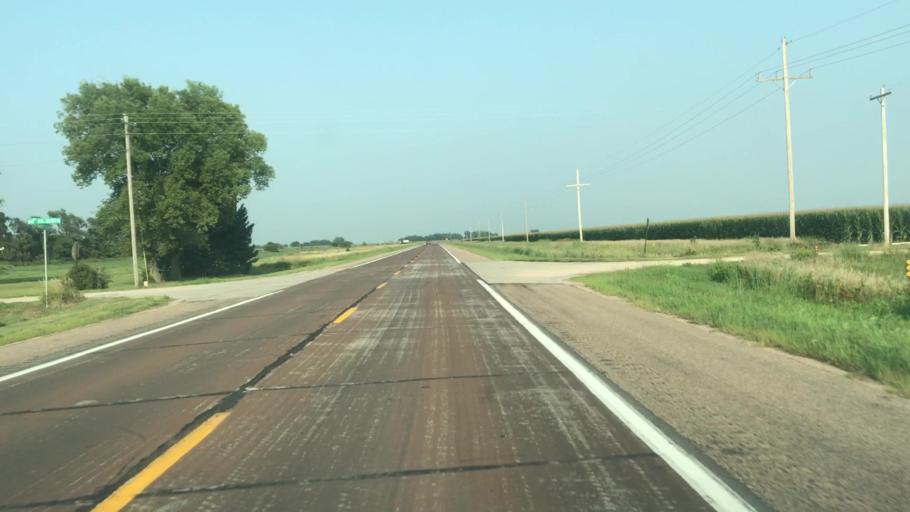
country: US
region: Nebraska
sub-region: Hall County
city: Grand Island
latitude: 40.9674
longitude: -98.4557
